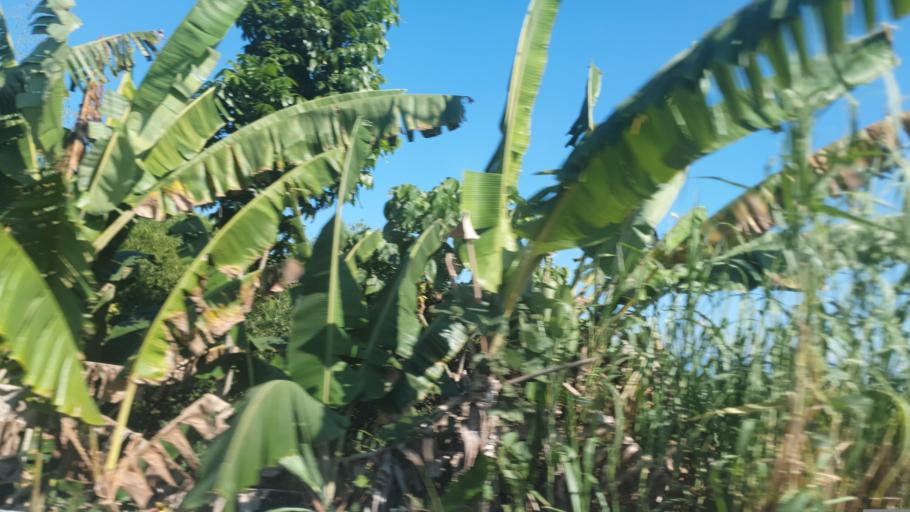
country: TW
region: Taiwan
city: Yujing
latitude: 23.0528
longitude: 120.4010
